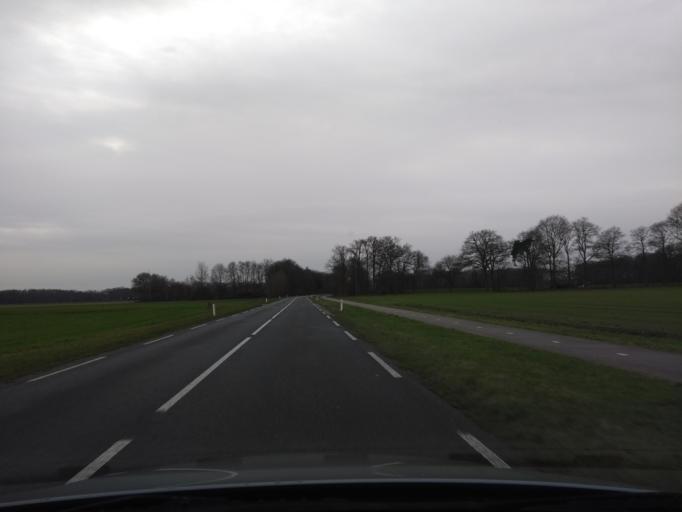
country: NL
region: Overijssel
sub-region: Gemeente Hof van Twente
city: Hengevelde
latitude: 52.1835
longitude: 6.6185
